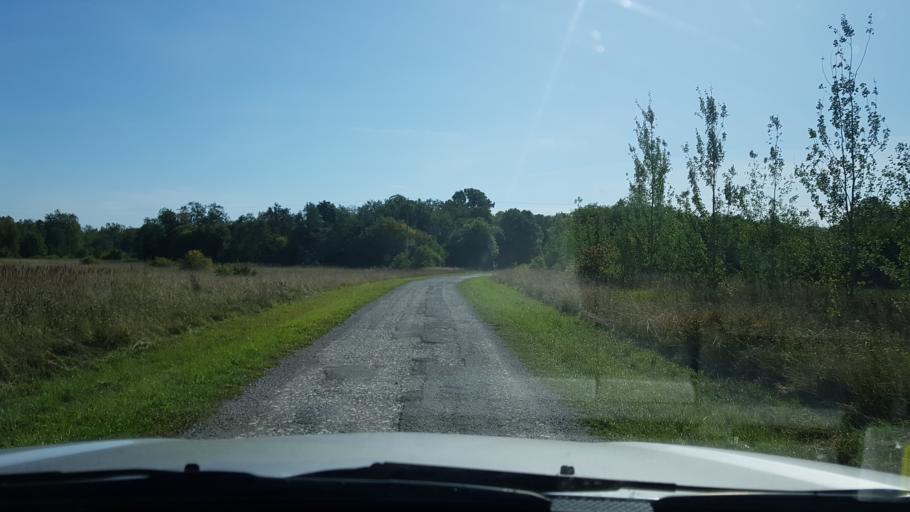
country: EE
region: Ida-Virumaa
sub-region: Sillamaee linn
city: Sillamae
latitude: 59.3911
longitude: 27.8771
